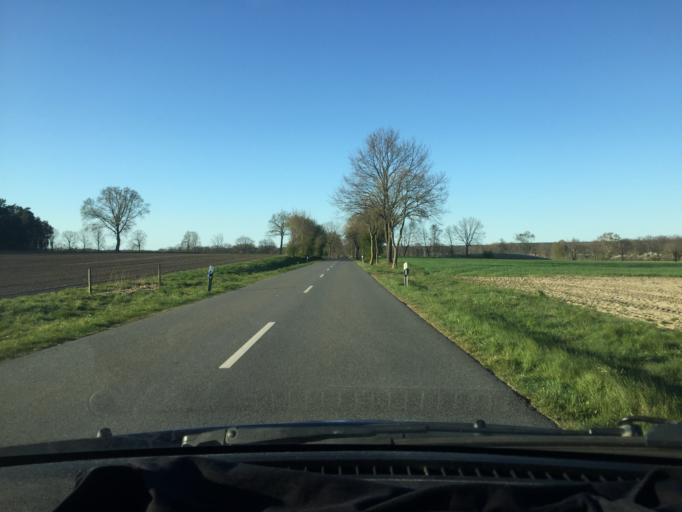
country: DE
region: Lower Saxony
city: Himbergen
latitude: 53.0778
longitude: 10.7302
